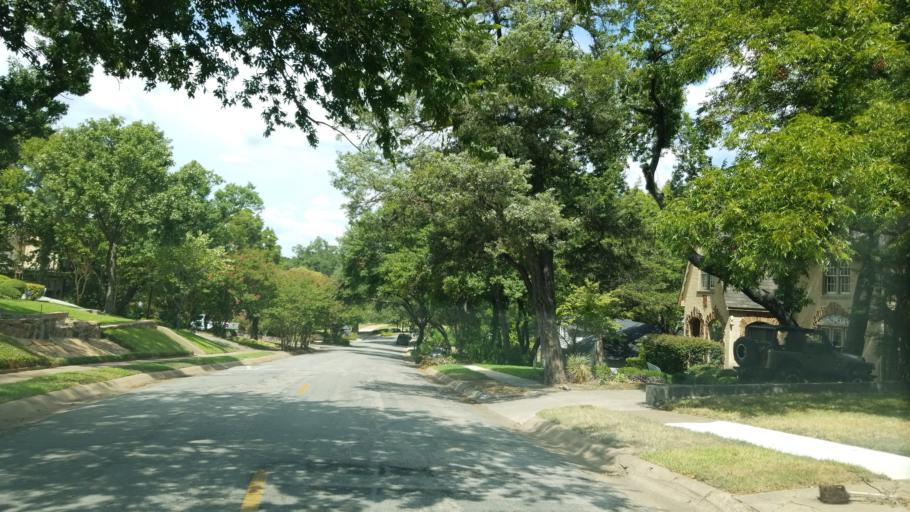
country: US
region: Texas
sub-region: Dallas County
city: Cockrell Hill
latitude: 32.7571
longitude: -96.8467
